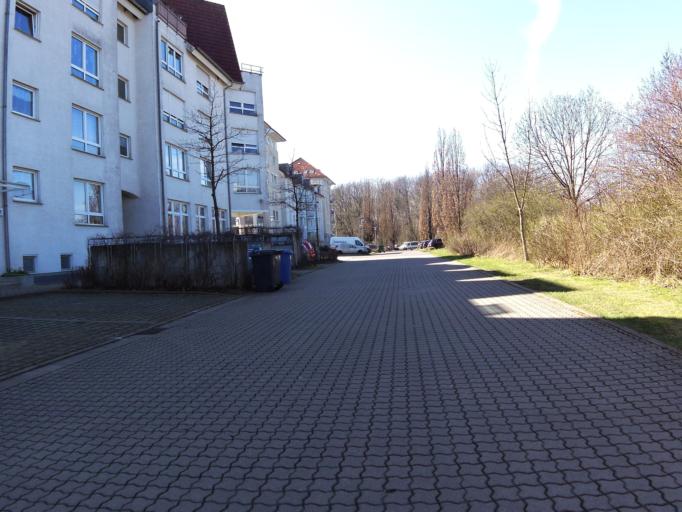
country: DE
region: Saxony
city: Taucha
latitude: 51.3598
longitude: 12.4697
